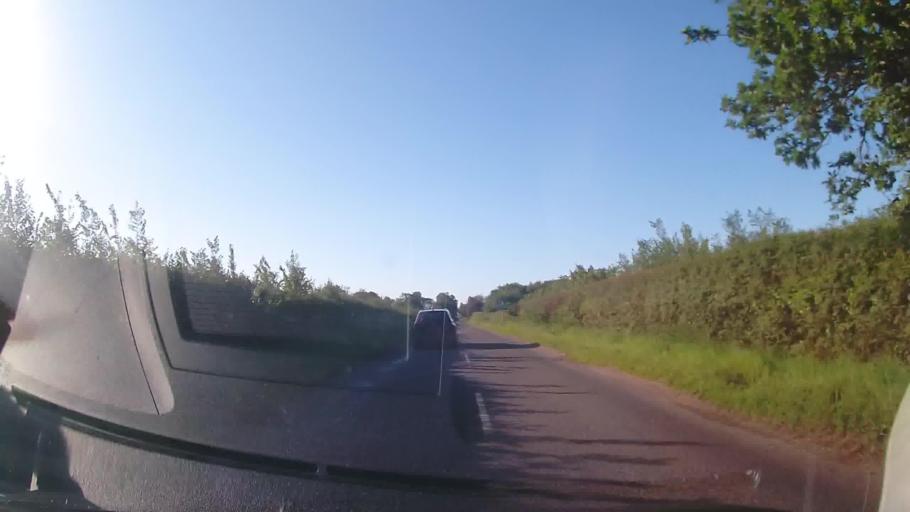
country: GB
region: England
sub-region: Shropshire
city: Shawbury
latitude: 52.7844
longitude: -2.6465
